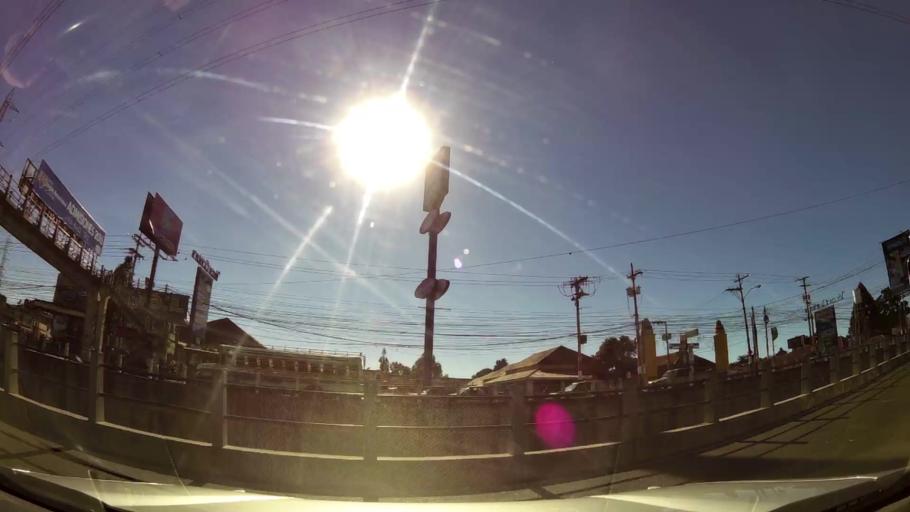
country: GT
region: Guatemala
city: San Jose Pinula
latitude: 14.5394
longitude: -90.4551
